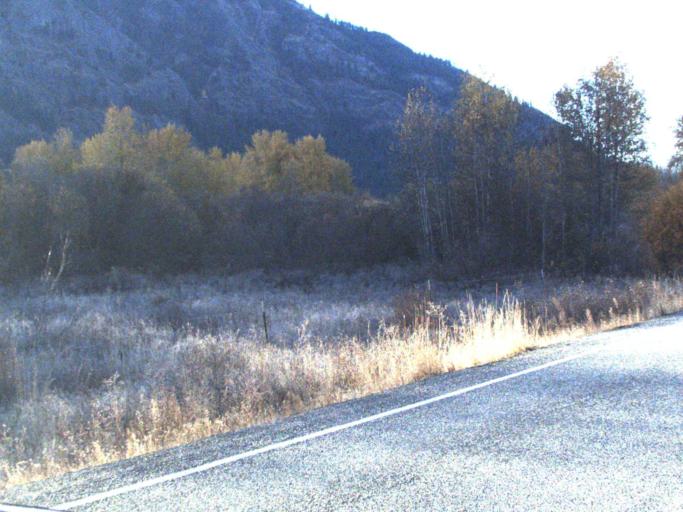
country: US
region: Washington
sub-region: Okanogan County
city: Coulee Dam
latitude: 48.2278
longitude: -118.7037
